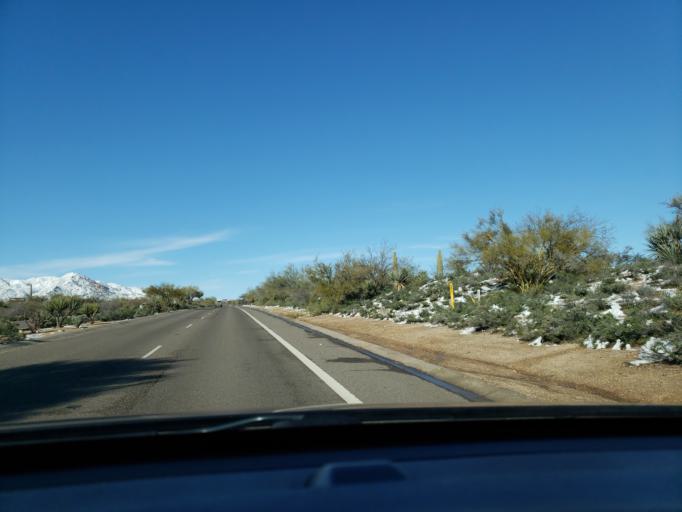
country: US
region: Arizona
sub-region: Maricopa County
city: Carefree
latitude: 33.8325
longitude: -111.8540
